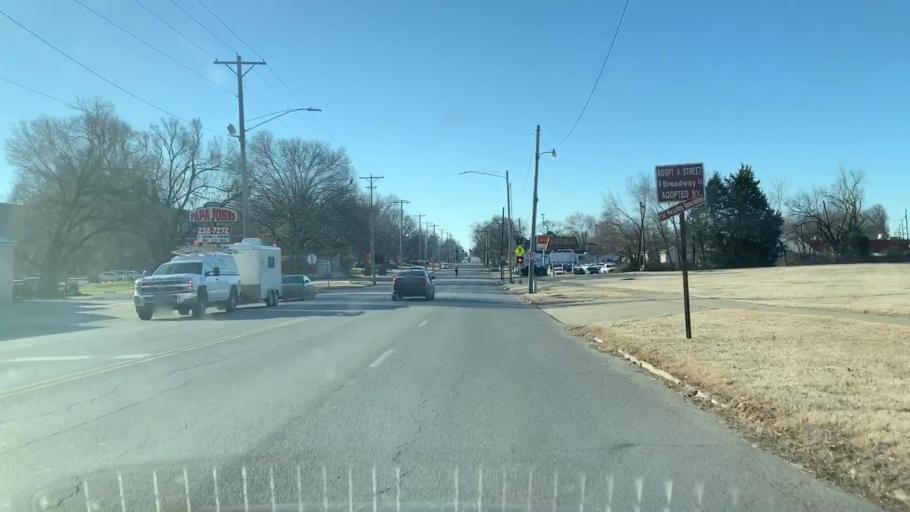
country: US
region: Kansas
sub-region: Crawford County
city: Pittsburg
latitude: 37.3940
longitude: -94.7051
